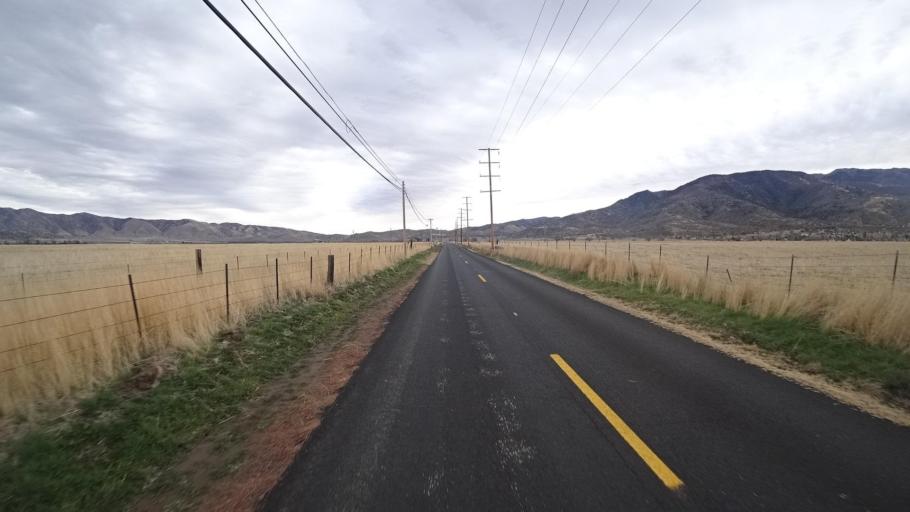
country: US
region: California
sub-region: Kern County
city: Stallion Springs
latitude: 35.0943
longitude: -118.6246
